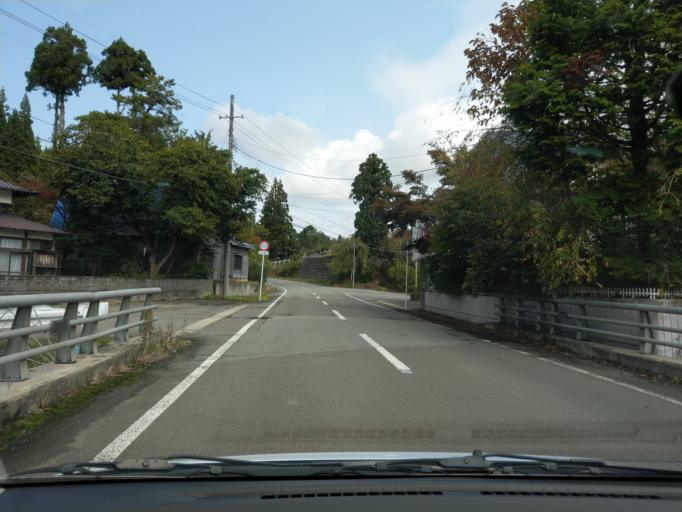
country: JP
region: Akita
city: Omagari
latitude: 39.5062
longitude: 140.3124
